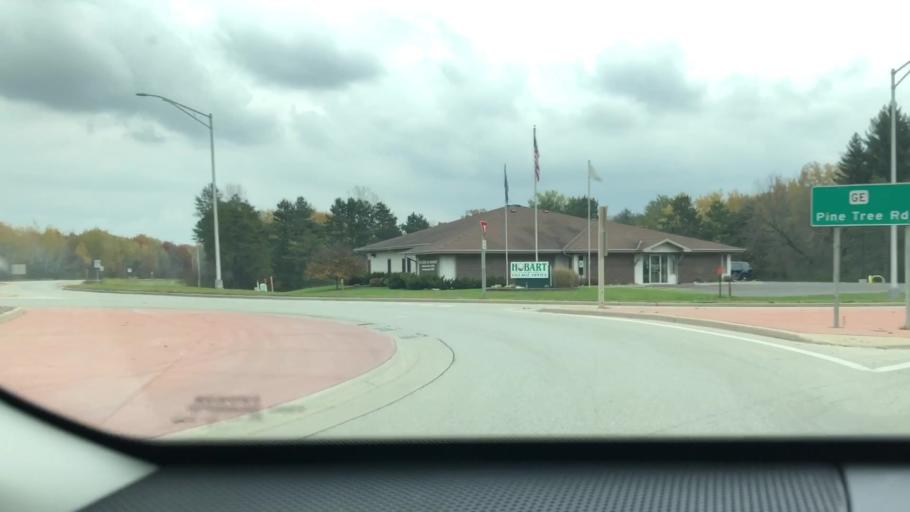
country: US
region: Wisconsin
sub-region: Brown County
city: Oneida
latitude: 44.4995
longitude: -88.1500
